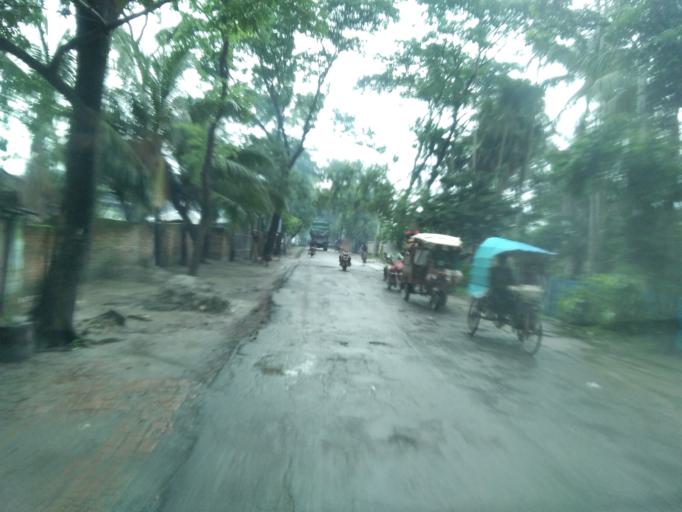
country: IN
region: West Bengal
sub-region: North 24 Parganas
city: Taki
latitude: 22.3505
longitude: 89.1030
